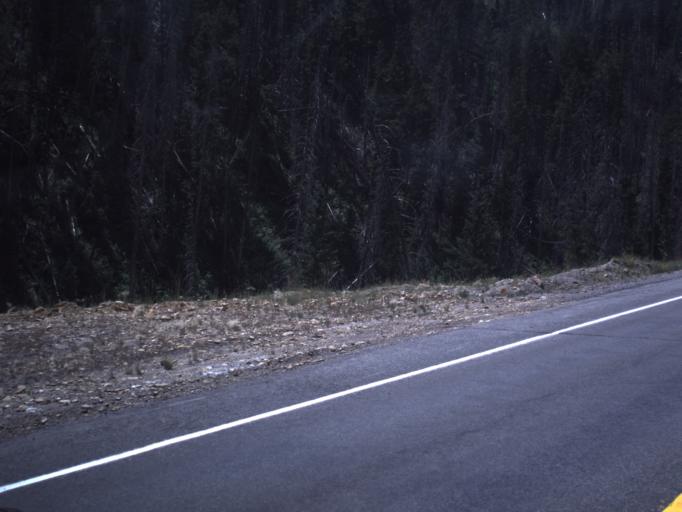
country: US
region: Utah
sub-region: Sanpete County
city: Fairview
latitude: 39.6823
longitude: -111.1866
